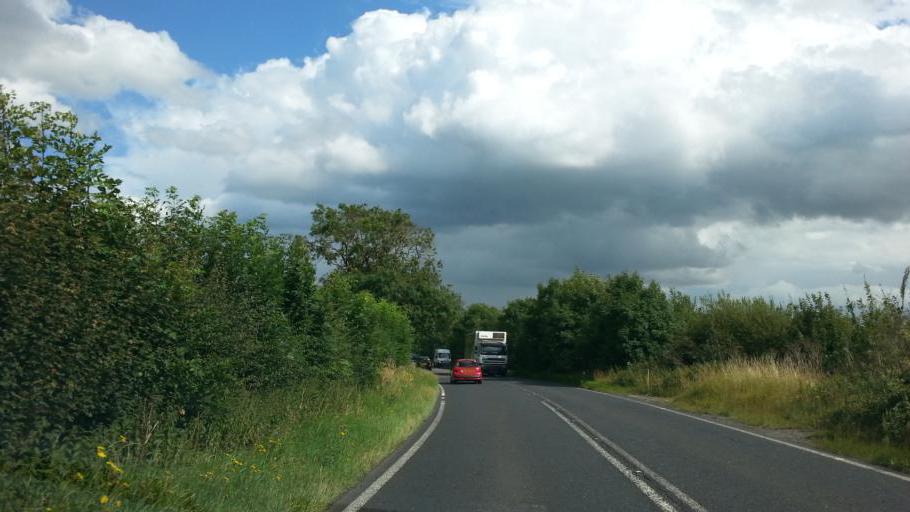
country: GB
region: England
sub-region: Nottinghamshire
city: Southwell
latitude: 53.1055
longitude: -0.9500
